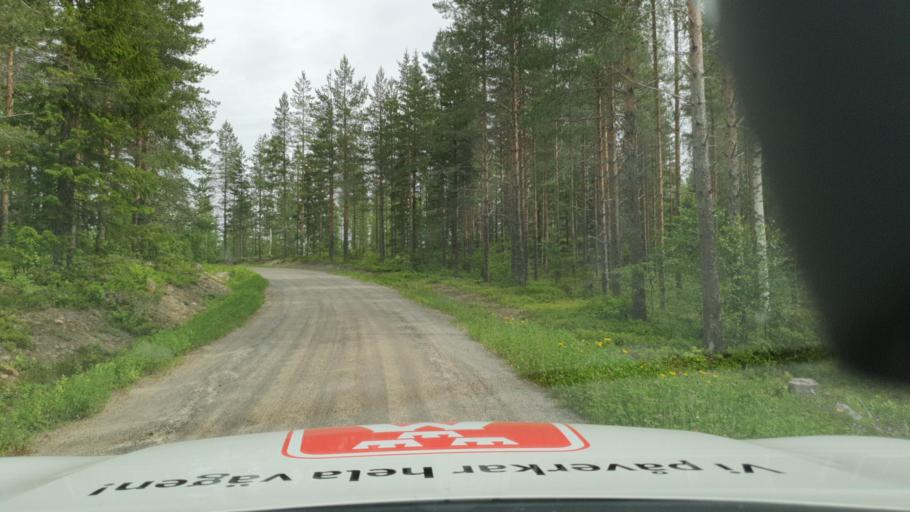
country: SE
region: Vaesterbotten
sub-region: Robertsfors Kommun
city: Robertsfors
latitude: 64.2642
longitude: 20.6887
